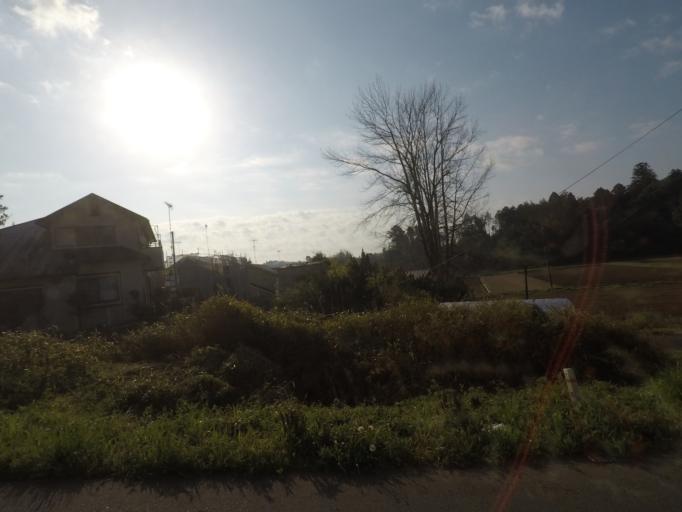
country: JP
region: Chiba
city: Yachimata
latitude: 35.6384
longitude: 140.2862
